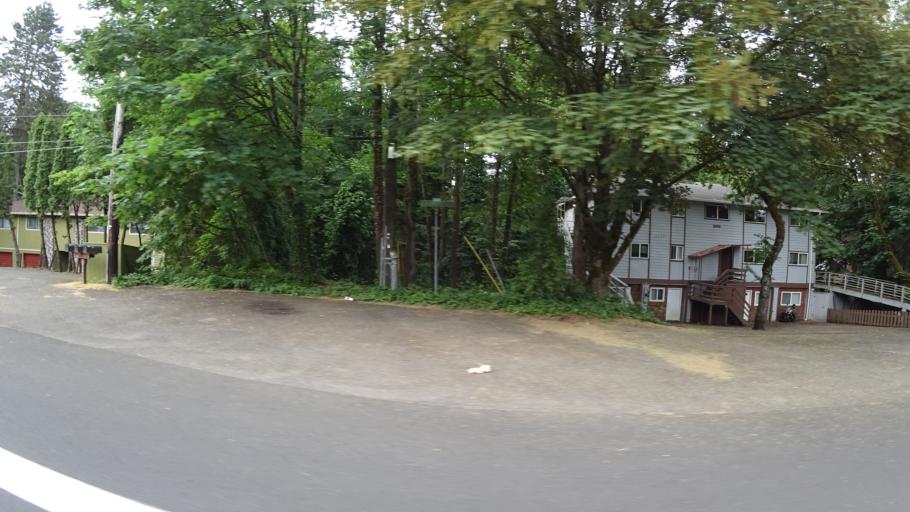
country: US
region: Oregon
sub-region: Multnomah County
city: Portland
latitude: 45.4802
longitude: -122.7040
